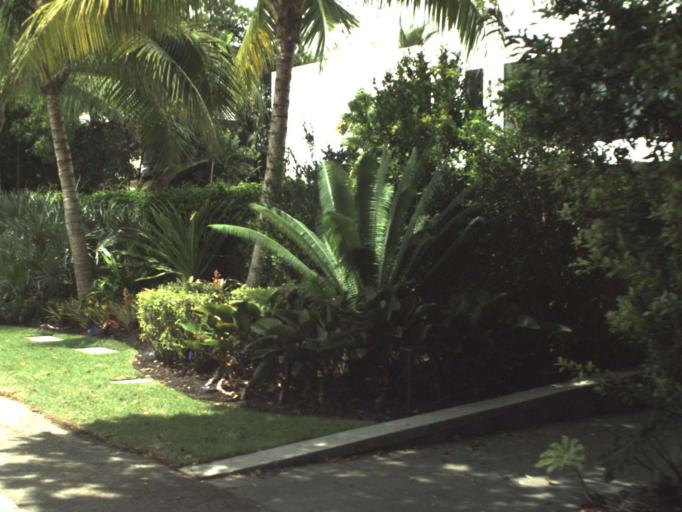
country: US
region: Florida
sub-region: Broward County
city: Hillsboro Beach
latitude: 26.2849
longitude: -80.0798
